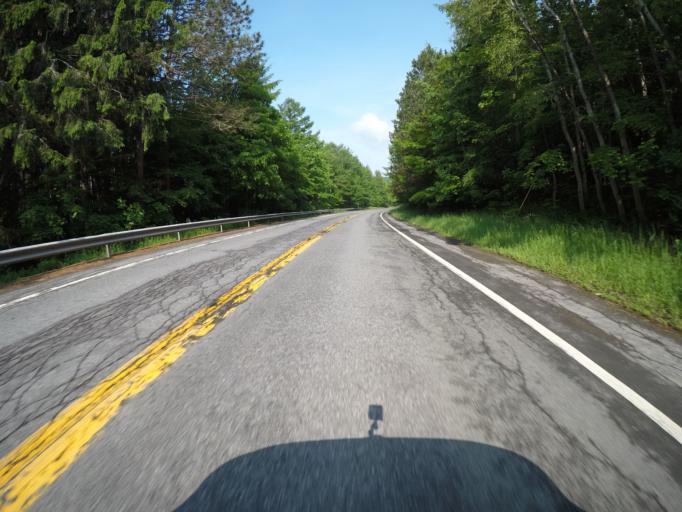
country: US
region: New York
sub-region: Sullivan County
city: Livingston Manor
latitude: 42.1201
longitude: -74.7315
